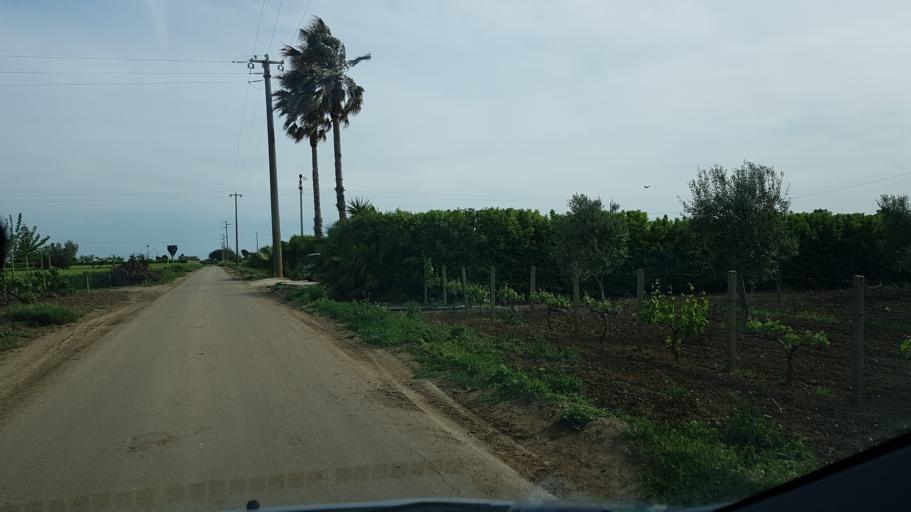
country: IT
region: Apulia
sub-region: Provincia di Brindisi
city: La Rosa
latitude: 40.5899
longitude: 17.9351
